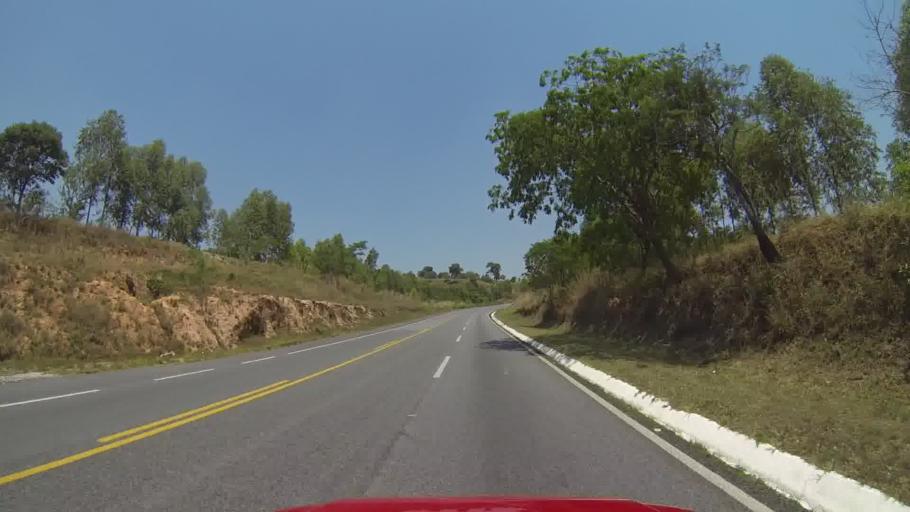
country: BR
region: Minas Gerais
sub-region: Itapecerica
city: Itapecerica
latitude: -20.2665
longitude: -45.1123
